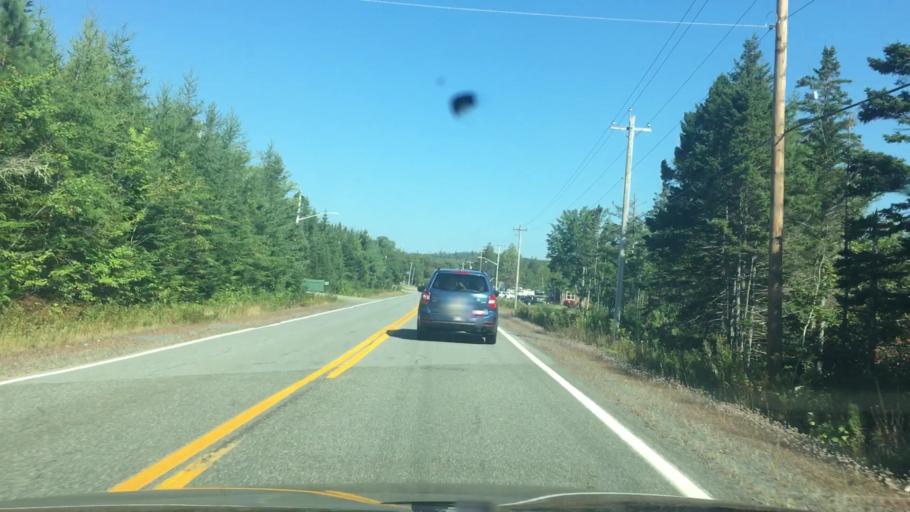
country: CA
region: Nova Scotia
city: Cole Harbour
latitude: 44.8034
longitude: -62.8805
